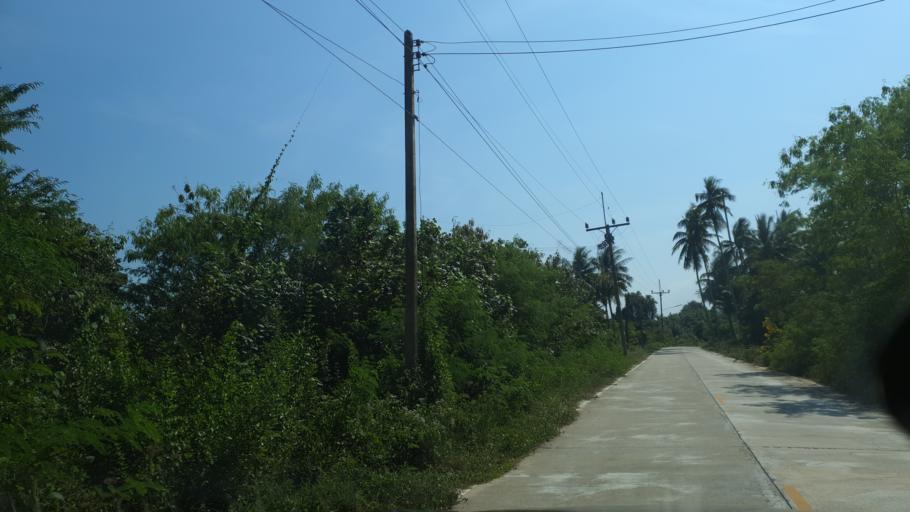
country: TH
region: Surat Thani
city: Tha Chana
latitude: 9.5998
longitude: 99.2060
